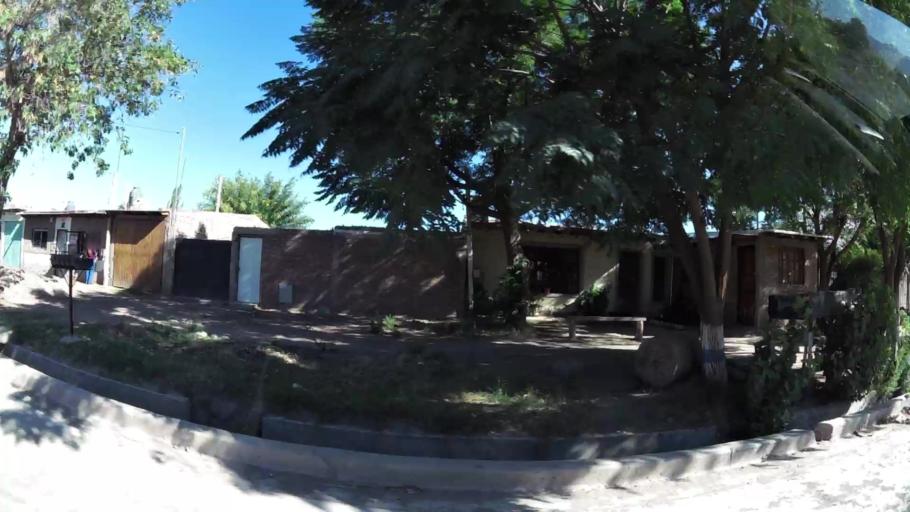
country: AR
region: Mendoza
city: Las Heras
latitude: -32.8325
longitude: -68.8275
